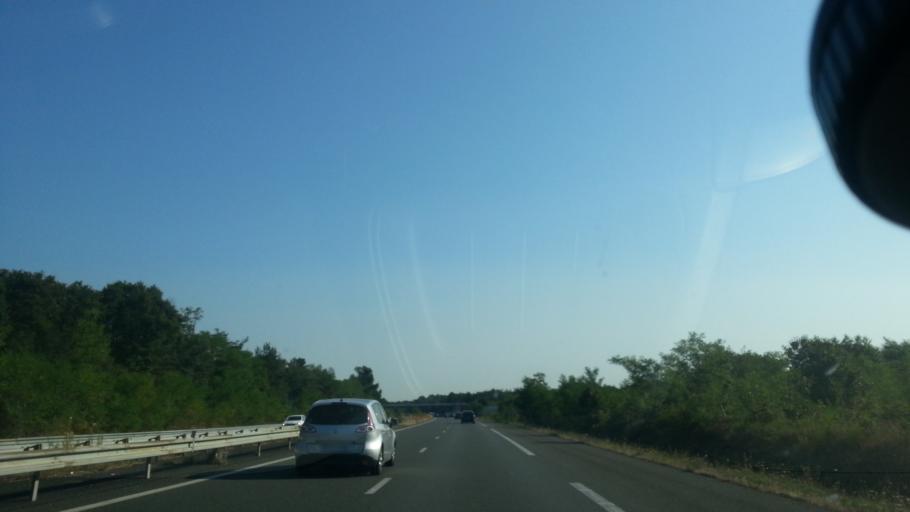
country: FR
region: Poitou-Charentes
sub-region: Departement de la Vienne
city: Naintre
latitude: 46.7850
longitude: 0.5044
